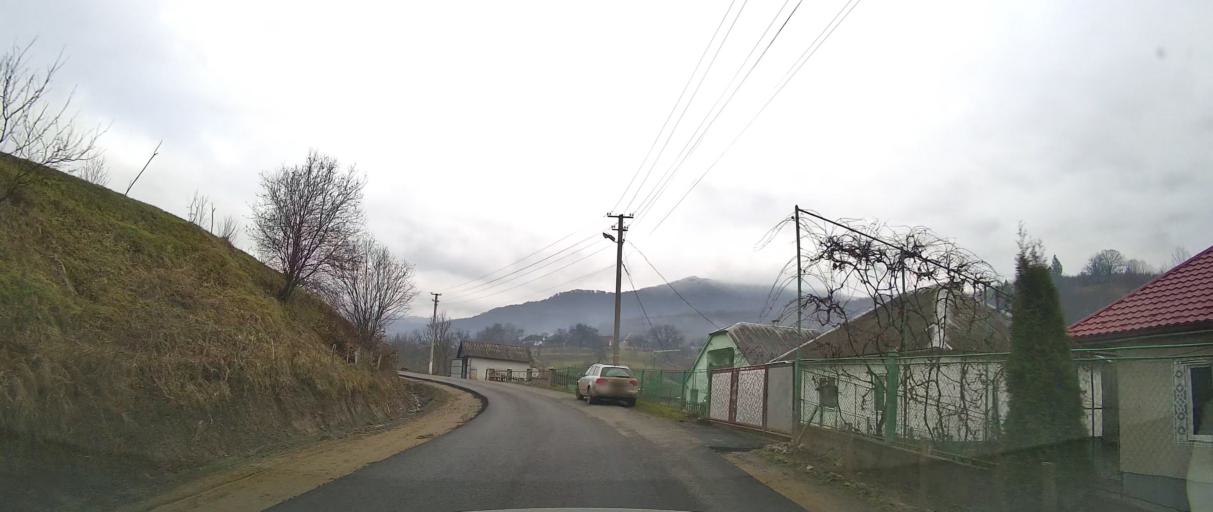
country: UA
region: Zakarpattia
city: Velykyi Bereznyi
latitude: 48.9619
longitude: 22.5491
